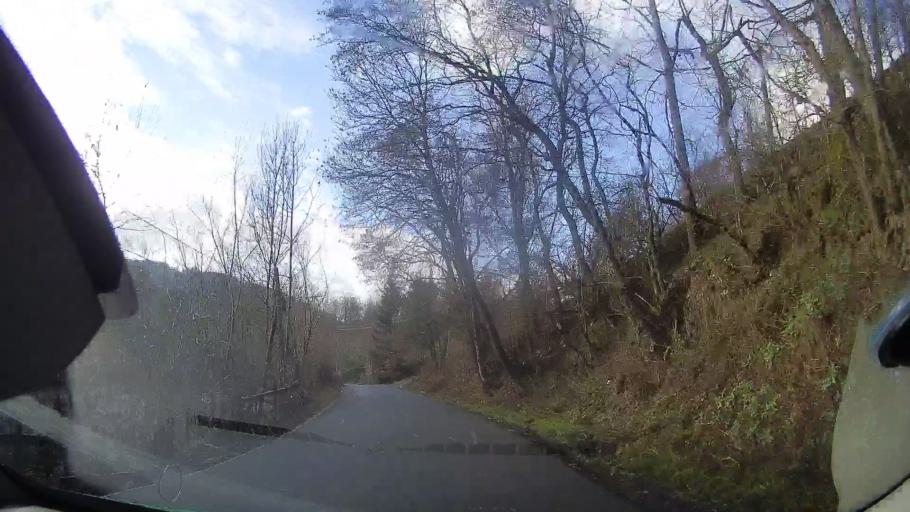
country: RO
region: Alba
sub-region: Comuna Sohodol
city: Sohodol
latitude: 46.3411
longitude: 23.0139
